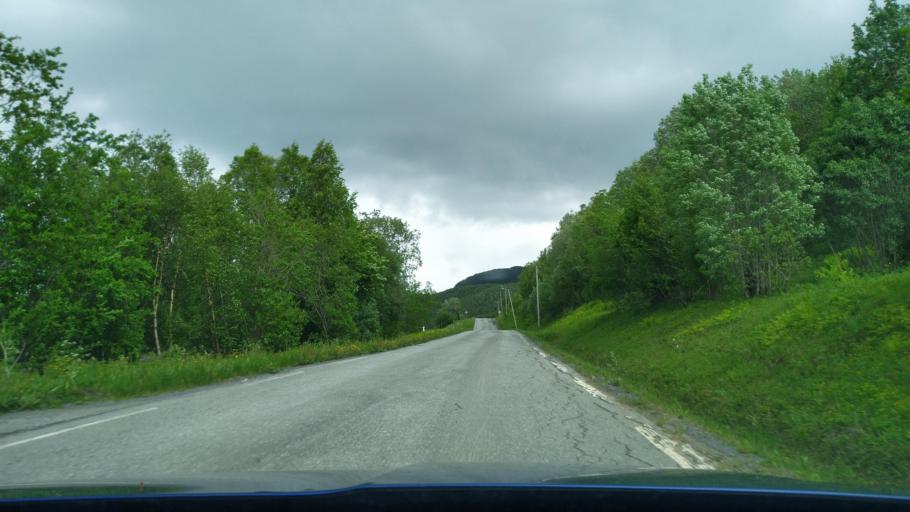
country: NO
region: Troms
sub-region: Lenvik
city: Finnsnes
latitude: 69.1317
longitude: 17.8757
